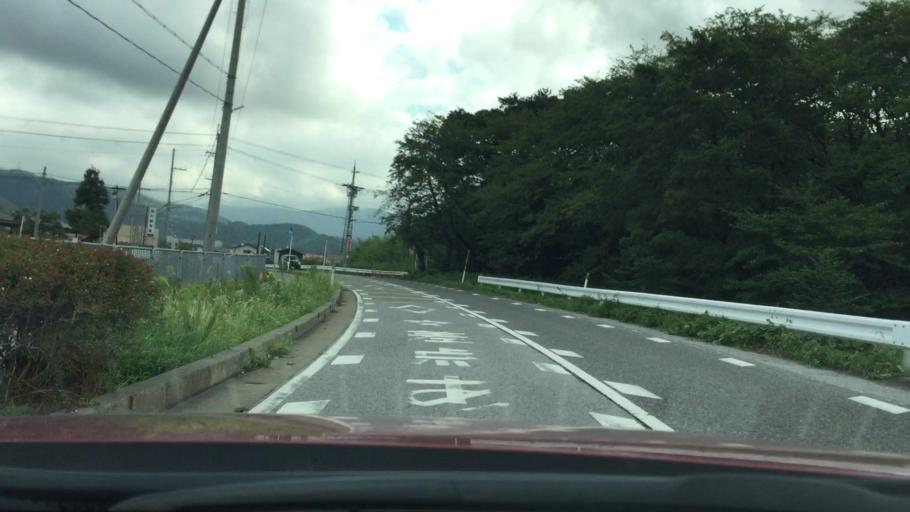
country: JP
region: Shiga Prefecture
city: Nagahama
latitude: 35.4253
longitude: 136.2944
